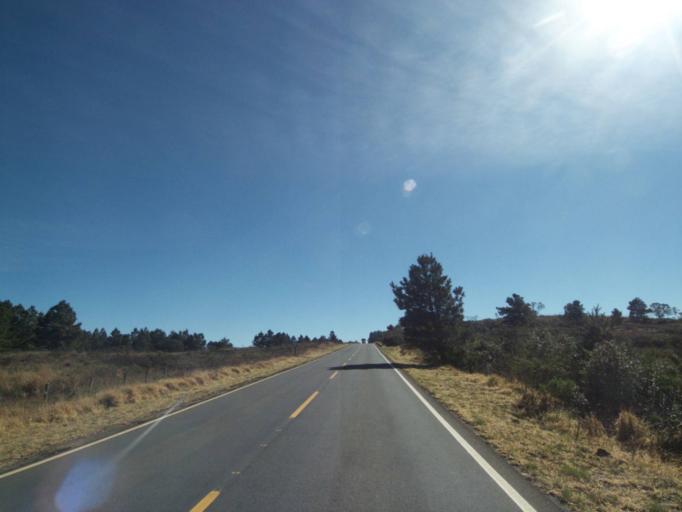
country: BR
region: Parana
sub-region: Castro
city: Castro
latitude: -24.7213
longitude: -50.1868
